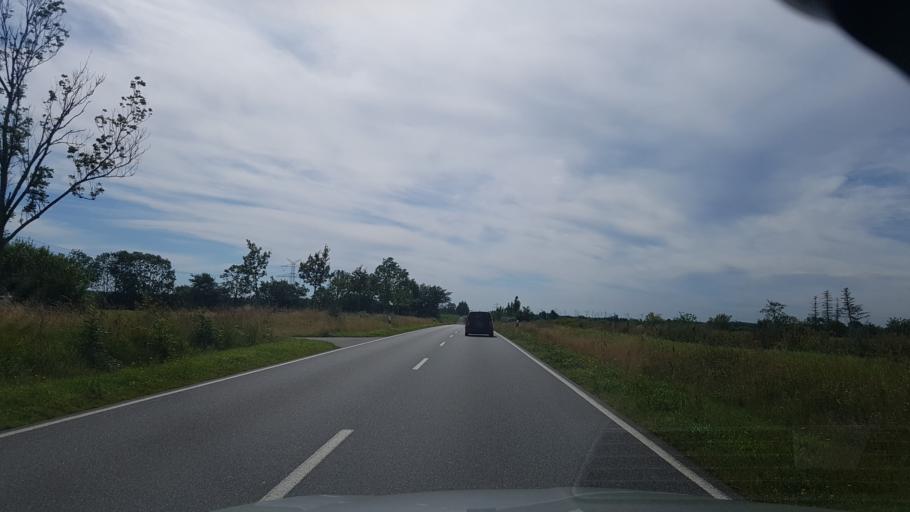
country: DE
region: Schleswig-Holstein
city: Osterby
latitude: 54.8162
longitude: 9.2274
